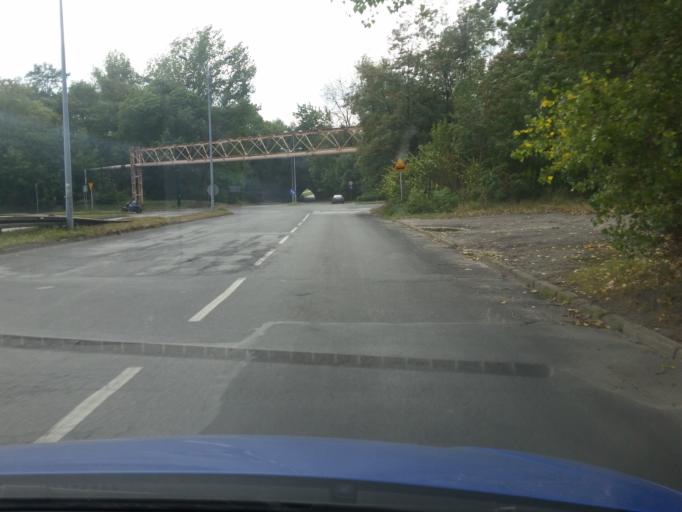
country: PL
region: Silesian Voivodeship
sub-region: Sosnowiec
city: Sosnowiec
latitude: 50.2532
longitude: 19.1259
